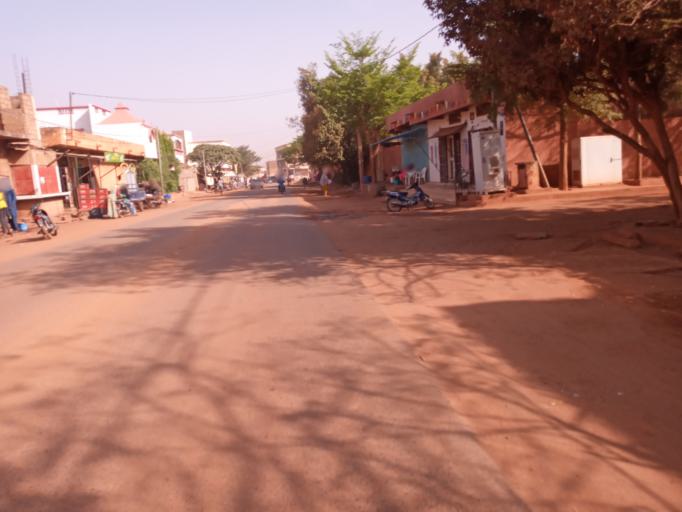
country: ML
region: Bamako
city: Bamako
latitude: 12.5816
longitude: -7.9579
